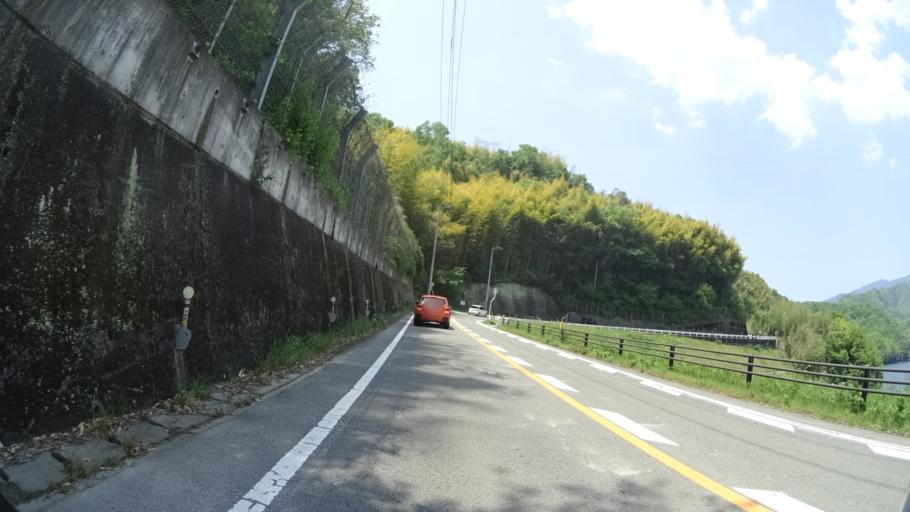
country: JP
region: Ehime
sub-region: Shikoku-chuo Shi
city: Matsuyama
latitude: 33.8809
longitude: 132.8376
